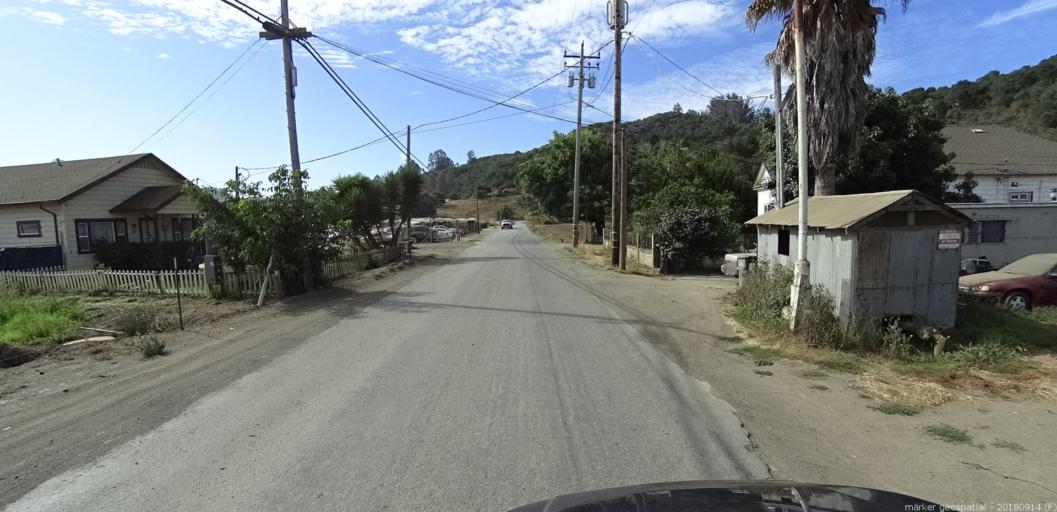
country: US
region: California
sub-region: San Benito County
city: Aromas
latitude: 36.8935
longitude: -121.6905
